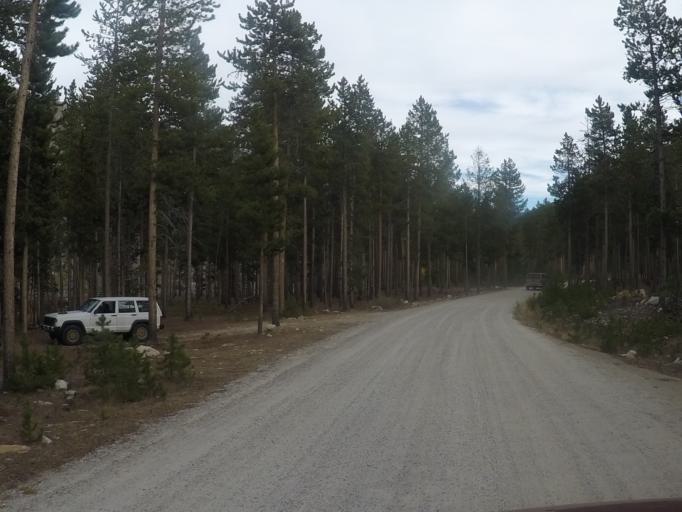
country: US
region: Montana
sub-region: Carbon County
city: Red Lodge
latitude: 45.1685
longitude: -109.4098
